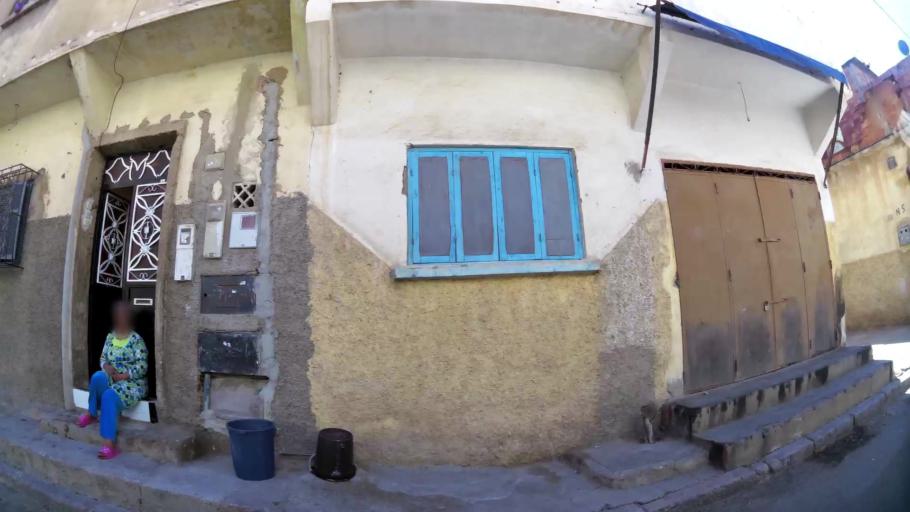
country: MA
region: Meknes-Tafilalet
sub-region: Meknes
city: Meknes
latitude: 33.9096
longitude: -5.5339
